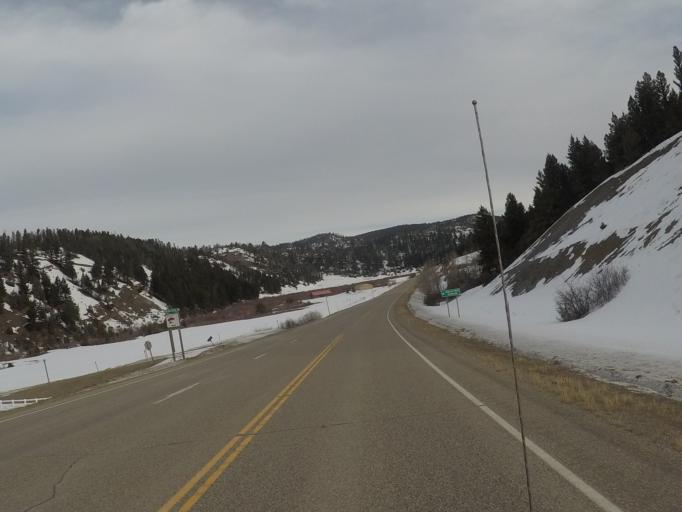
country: US
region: Montana
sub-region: Meagher County
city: White Sulphur Springs
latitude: 46.6685
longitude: -110.8773
